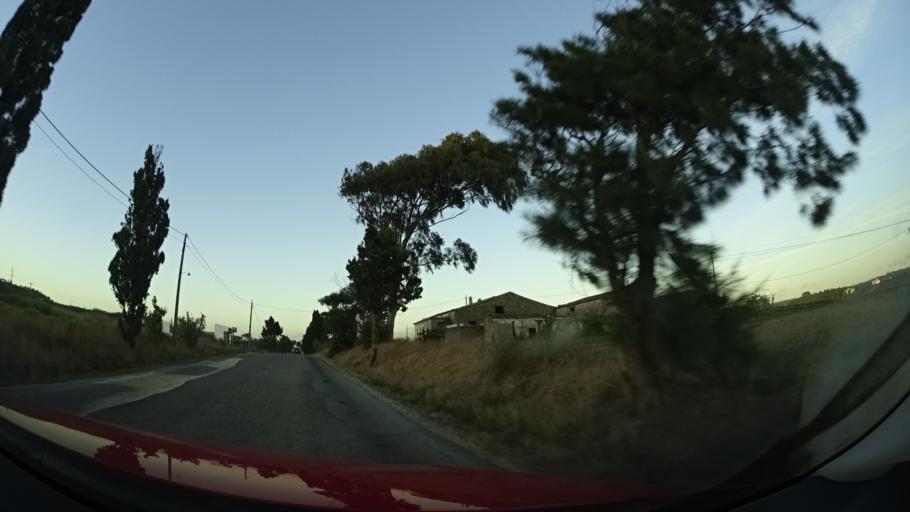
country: PT
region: Faro
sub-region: Aljezur
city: Aljezur
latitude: 37.2265
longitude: -8.8323
